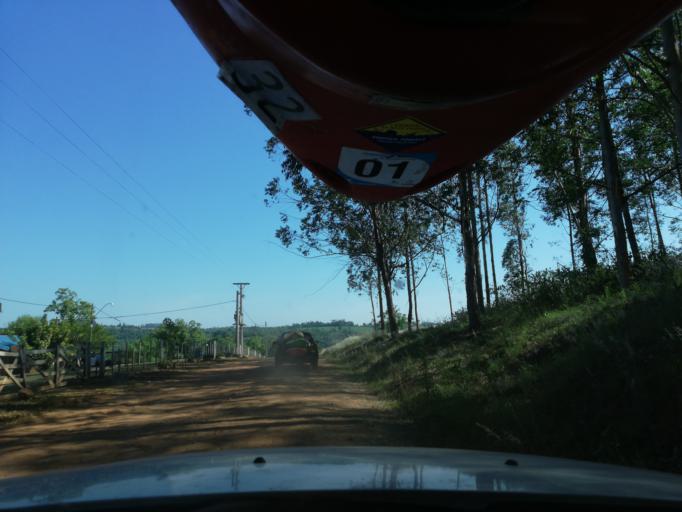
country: AR
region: Misiones
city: Puerto Leoni
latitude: -26.9622
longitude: -55.1526
